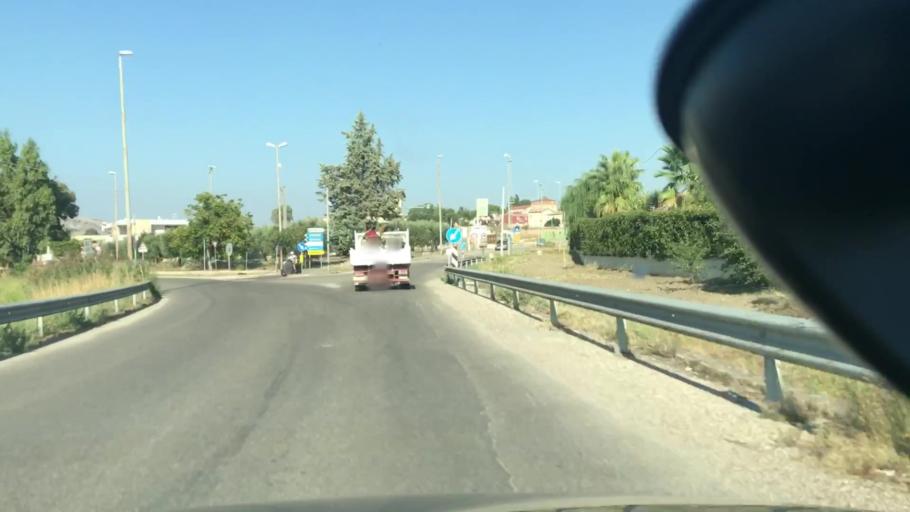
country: IT
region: Basilicate
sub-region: Provincia di Matera
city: La Martella
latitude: 40.6590
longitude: 16.5415
